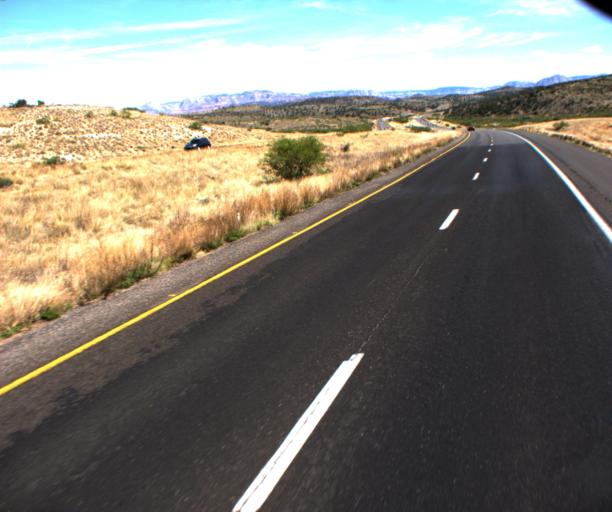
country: US
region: Arizona
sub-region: Yavapai County
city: Cornville
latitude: 34.7752
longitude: -111.9303
